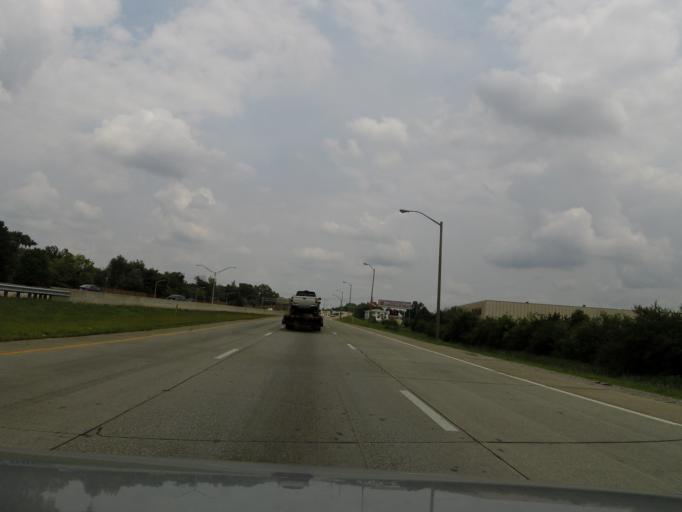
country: US
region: Kentucky
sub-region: Jefferson County
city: Audubon Park
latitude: 38.1905
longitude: -85.7228
